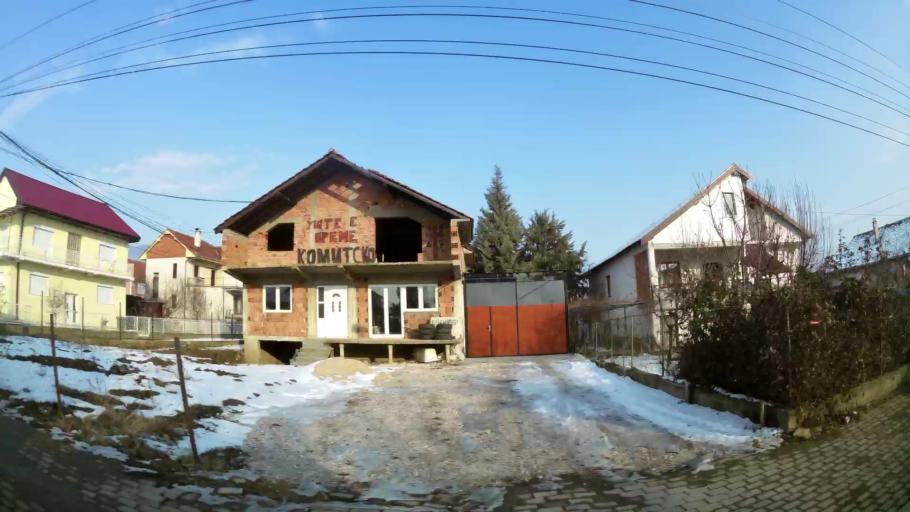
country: MK
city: Creshevo
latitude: 42.0289
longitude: 21.5126
